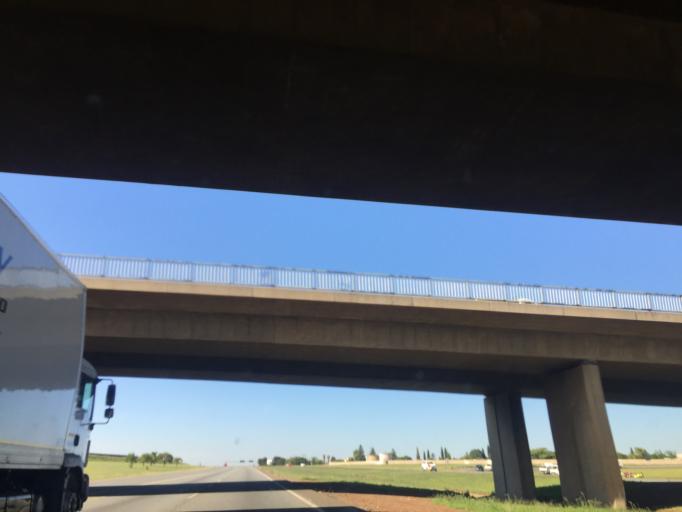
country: ZA
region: Gauteng
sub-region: Ekurhuleni Metropolitan Municipality
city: Germiston
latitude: -26.3514
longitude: 28.1002
